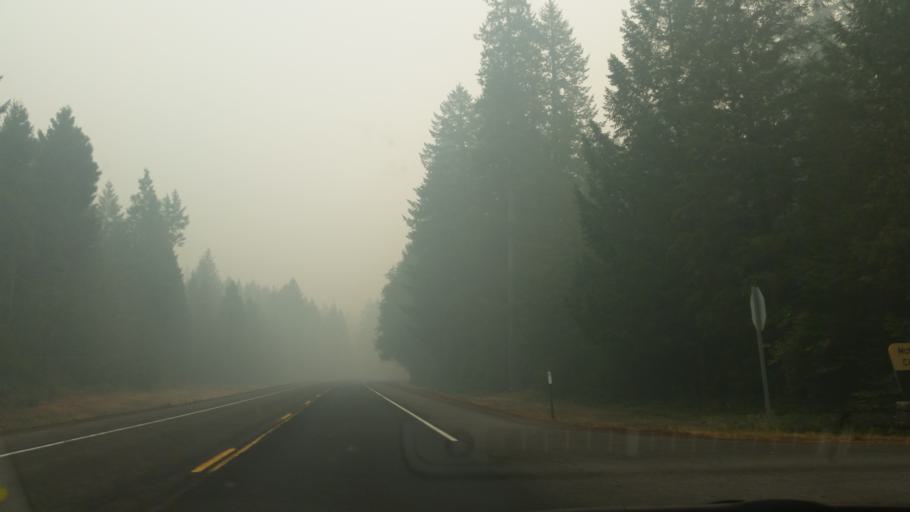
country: US
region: Oregon
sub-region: Lane County
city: Oakridge
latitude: 44.1769
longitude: -122.1743
